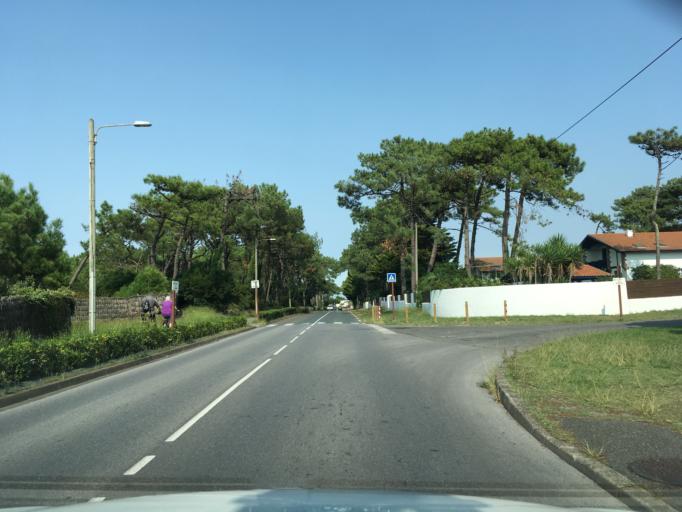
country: FR
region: Aquitaine
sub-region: Departement des Pyrenees-Atlantiques
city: Anglet
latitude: 43.5221
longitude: -1.5208
